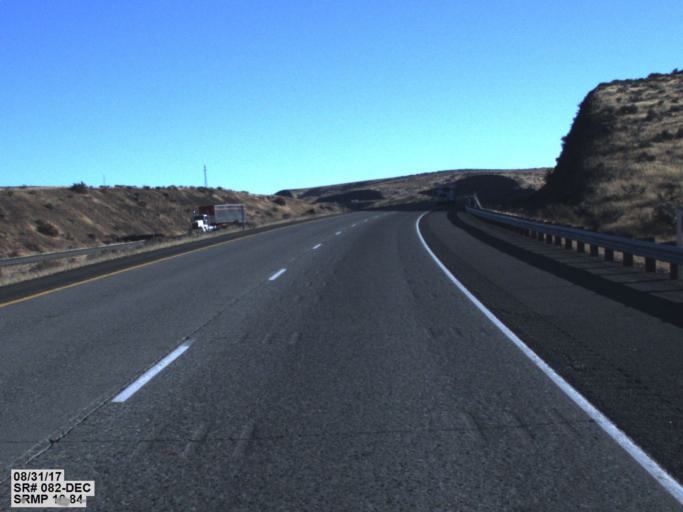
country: US
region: Washington
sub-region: Yakima County
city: Terrace Heights
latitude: 46.7519
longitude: -120.3876
